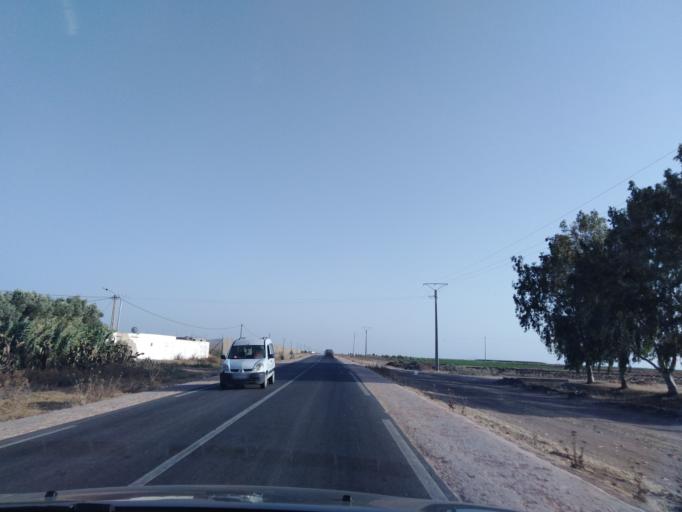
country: MA
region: Doukkala-Abda
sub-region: El-Jadida
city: Sidi Bennour
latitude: 32.5189
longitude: -8.7422
